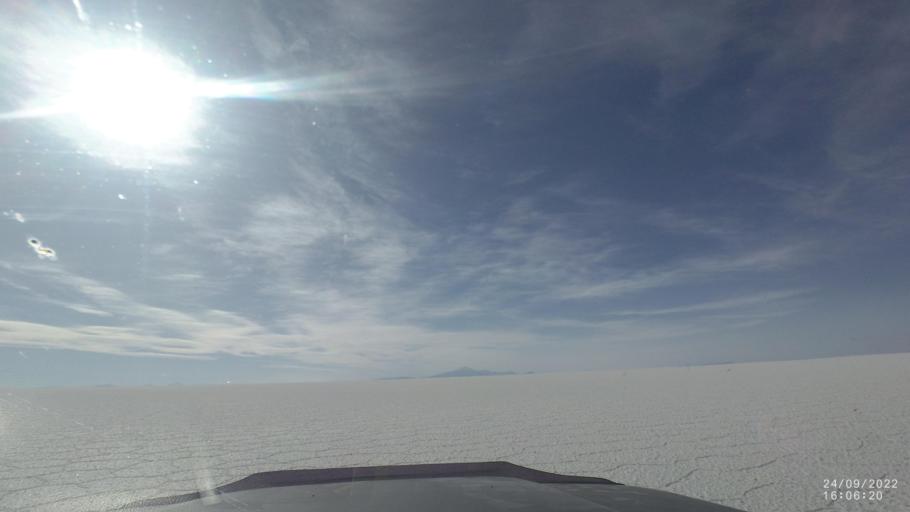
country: BO
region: Potosi
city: Colchani
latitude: -20.3068
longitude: -67.2931
